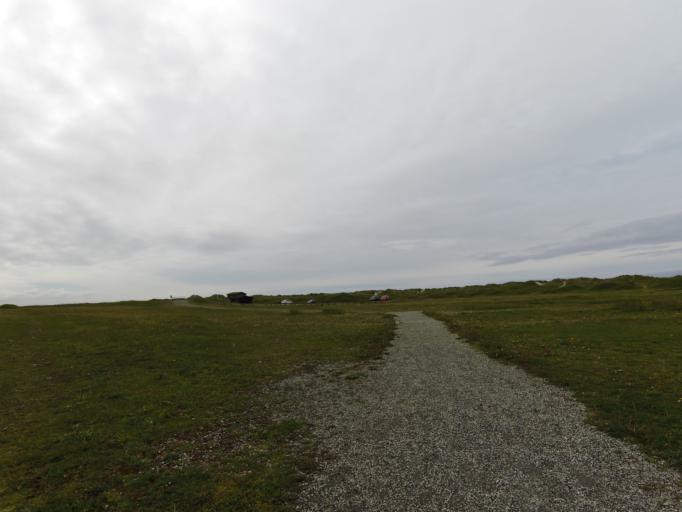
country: NO
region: Rogaland
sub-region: Klepp
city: Kleppe
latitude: 58.8106
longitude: 5.5514
